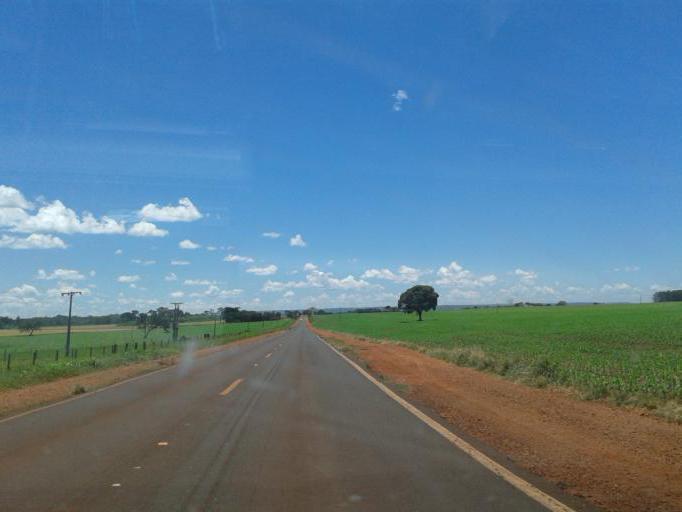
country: BR
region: Minas Gerais
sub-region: Capinopolis
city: Capinopolis
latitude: -18.6046
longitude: -49.5243
